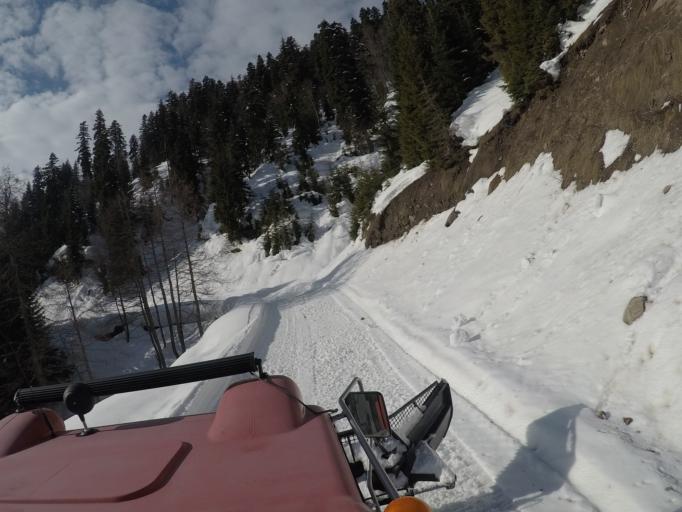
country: GE
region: Samtskhe-Javakheti
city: Adigeni
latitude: 41.6358
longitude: 42.5792
